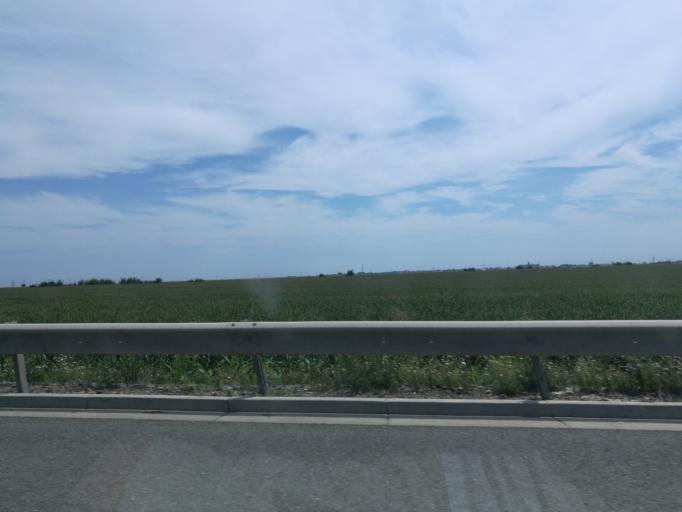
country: RO
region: Constanta
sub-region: Municipiul Constanta
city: Palazu Mare
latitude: 44.1896
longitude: 28.5512
